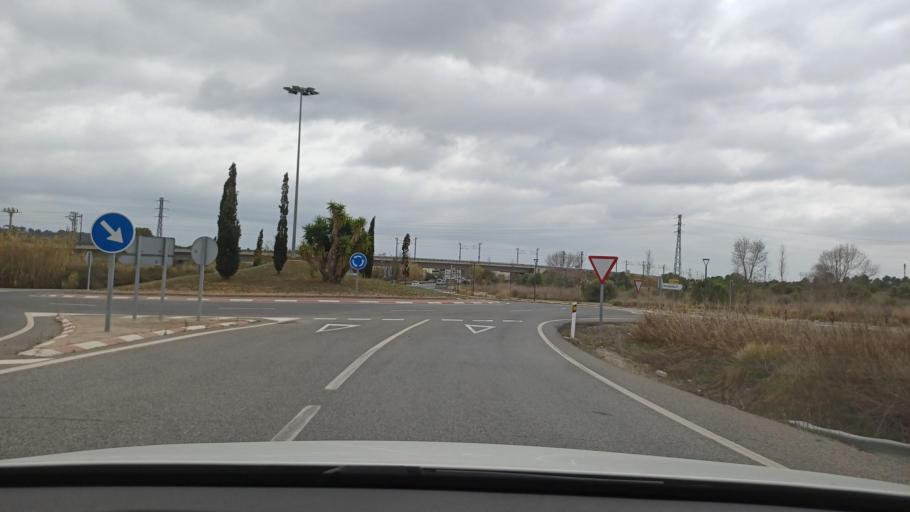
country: ES
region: Catalonia
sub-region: Provincia de Tarragona
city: la Pobla de Mafumet
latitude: 41.1936
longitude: 1.2431
